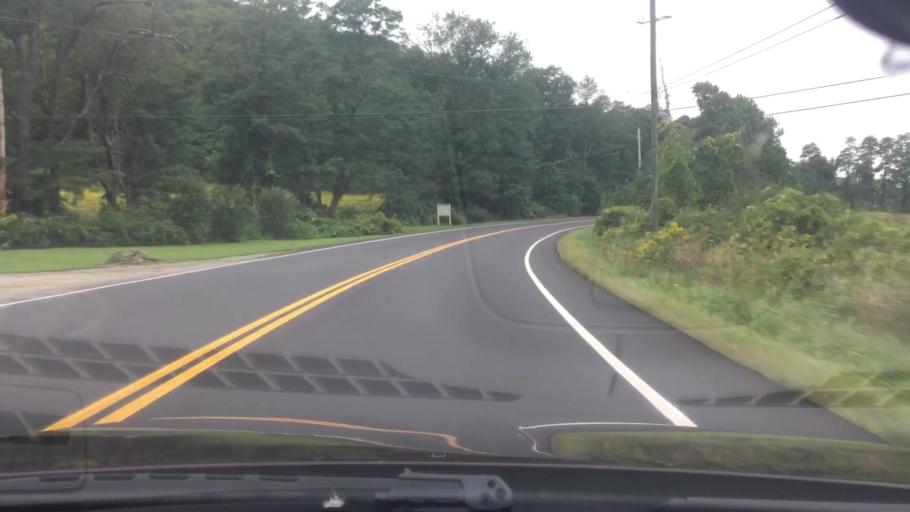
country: US
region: New York
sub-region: Dutchess County
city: Dover Plains
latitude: 41.8435
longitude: -73.5946
